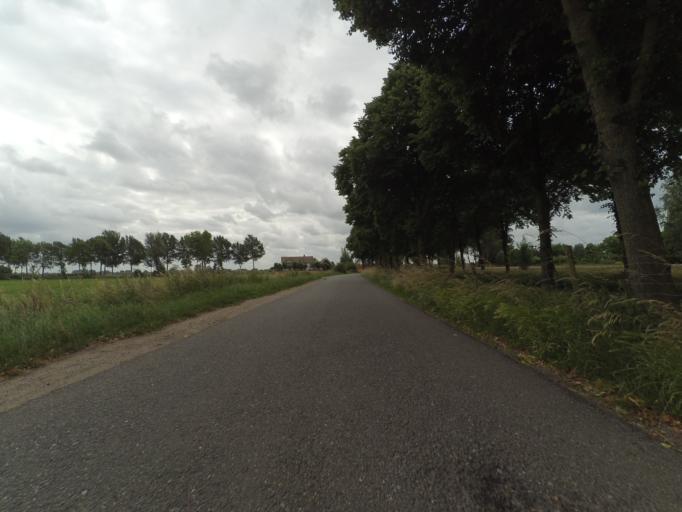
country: NL
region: South Holland
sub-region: Gemeente Gorinchem
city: Gorinchem
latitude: 51.8740
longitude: 5.0059
